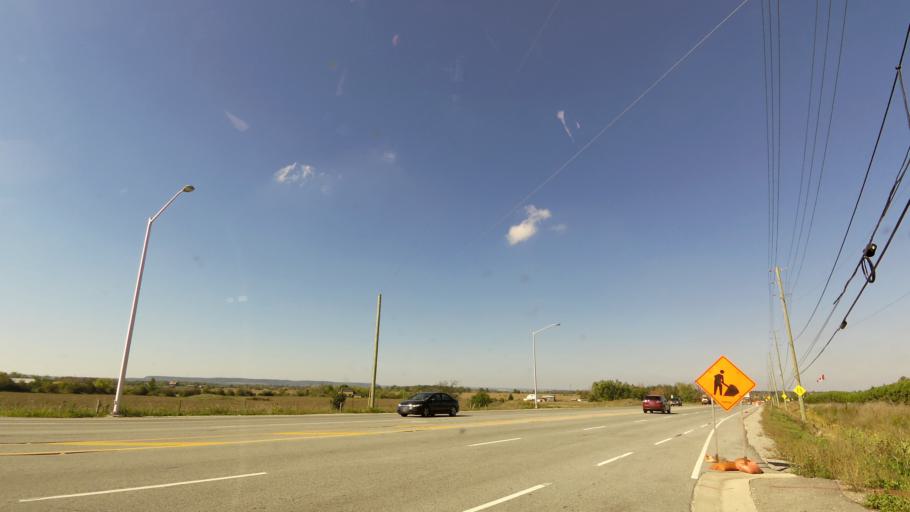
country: CA
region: Ontario
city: Burlington
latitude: 43.4624
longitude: -79.8059
